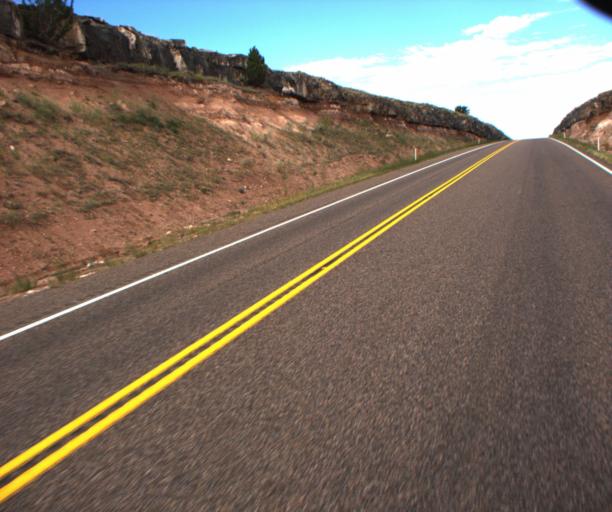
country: US
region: Arizona
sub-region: Apache County
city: Springerville
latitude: 34.1501
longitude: -109.1748
